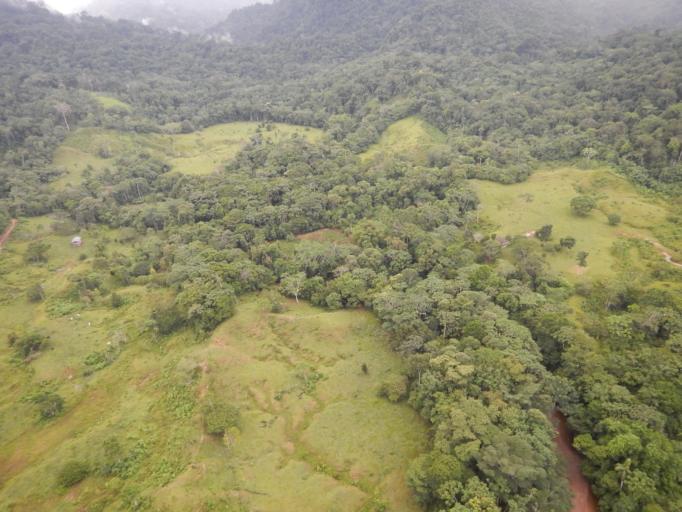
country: BO
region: Santa Cruz
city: Comarapa
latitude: -17.2709
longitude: -64.5558
